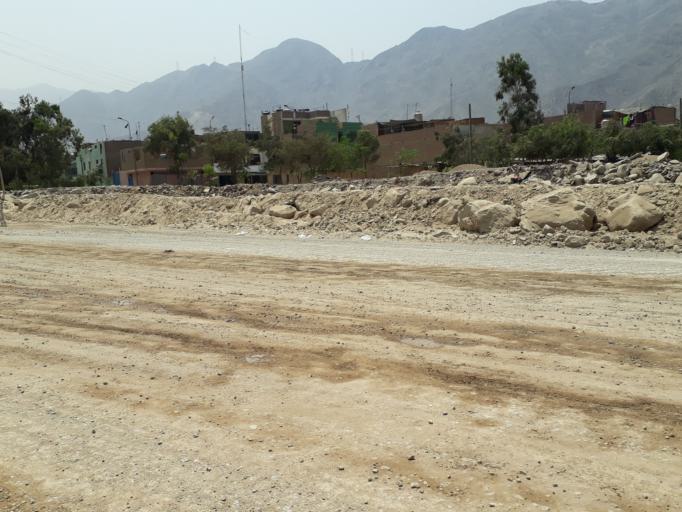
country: PE
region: Lima
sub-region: Lima
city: Santa Maria
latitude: -11.9877
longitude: -76.9013
